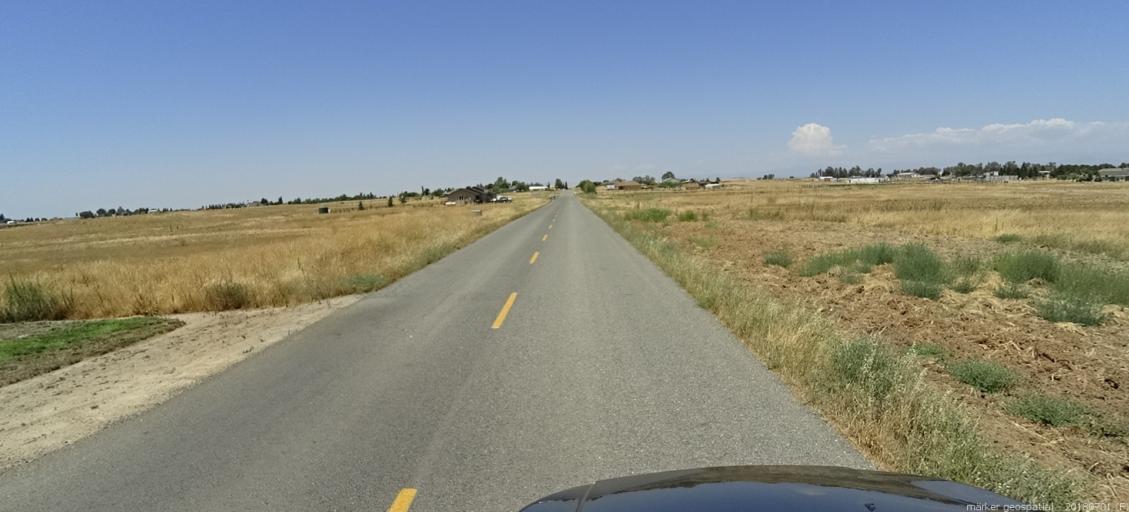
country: US
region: California
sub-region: Madera County
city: Madera Acres
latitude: 37.0592
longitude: -120.0112
